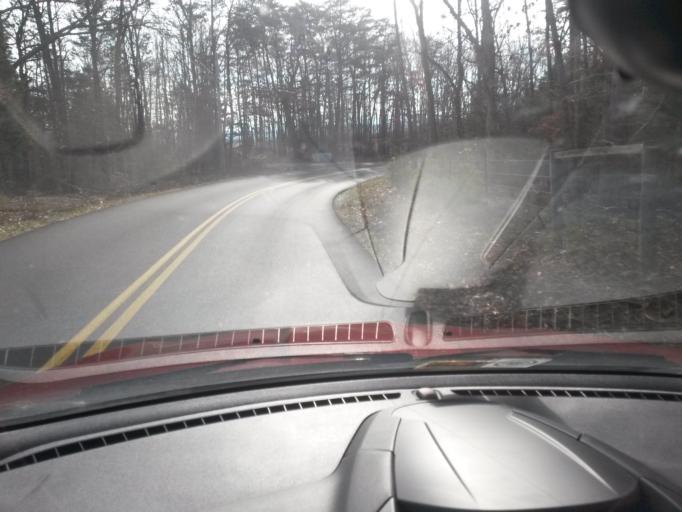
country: US
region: Virginia
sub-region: Botetourt County
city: Fincastle
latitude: 37.5451
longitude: -79.8746
